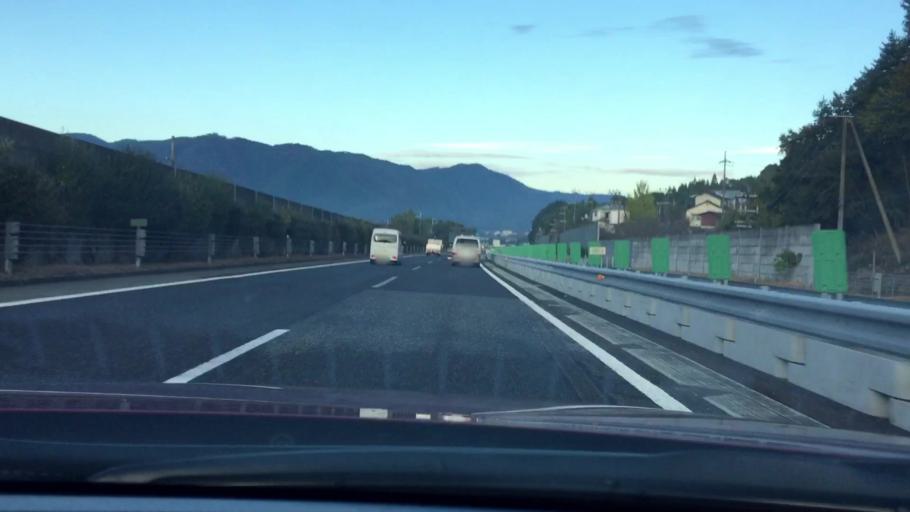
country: JP
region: Hyogo
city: Yamazakicho-nakabirose
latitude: 34.9953
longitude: 134.5656
